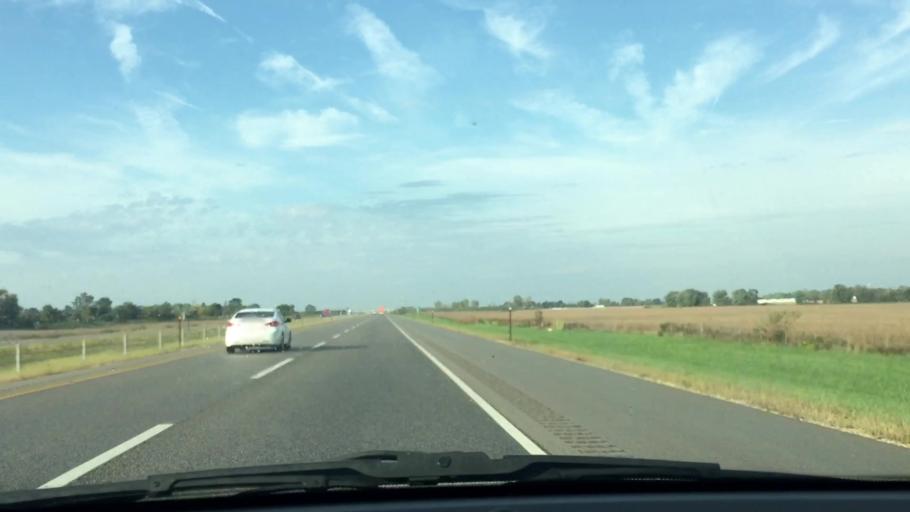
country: US
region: Illinois
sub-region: Lee County
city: Franklin Grove
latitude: 41.8621
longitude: -89.1935
